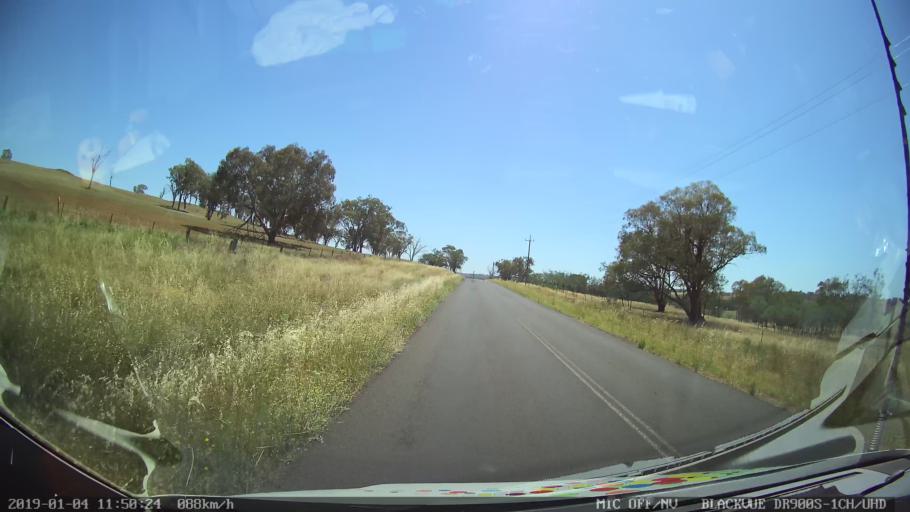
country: AU
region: New South Wales
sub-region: Cabonne
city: Molong
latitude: -32.9067
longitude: 148.7567
